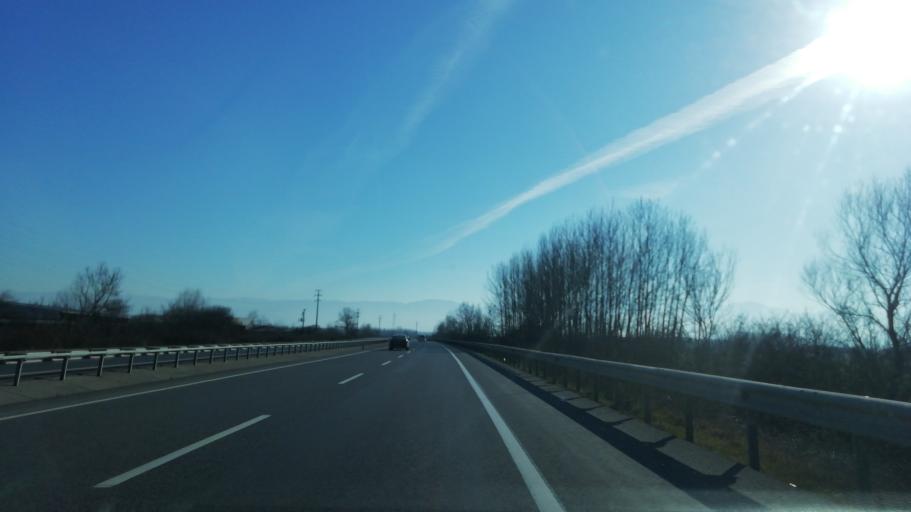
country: TR
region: Sakarya
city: Akyazi
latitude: 40.7400
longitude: 30.5642
